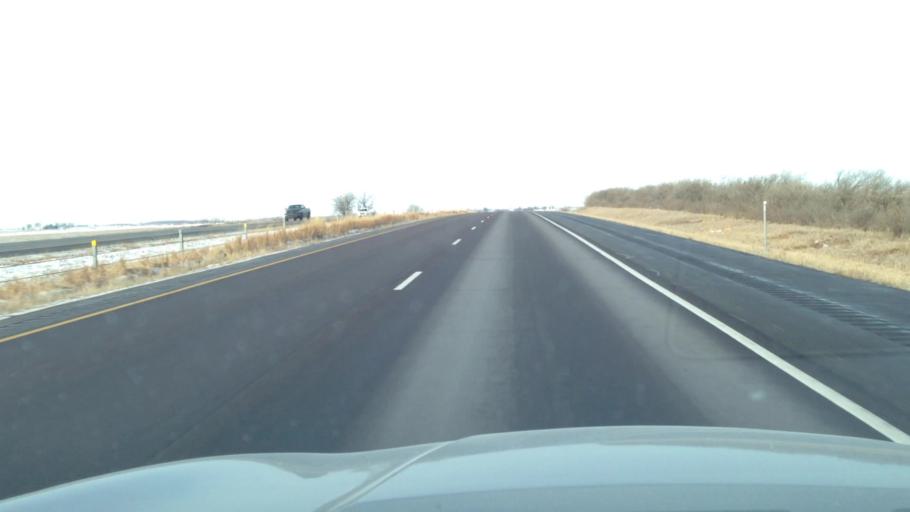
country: US
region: Iowa
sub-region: Poweshiek County
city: Grinnell
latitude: 41.6959
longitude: -92.6563
